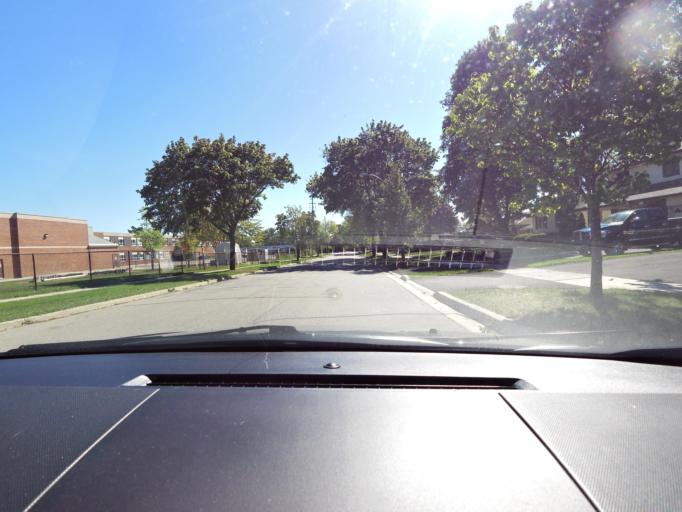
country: CA
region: Ontario
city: Burlington
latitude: 43.3541
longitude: -79.8141
